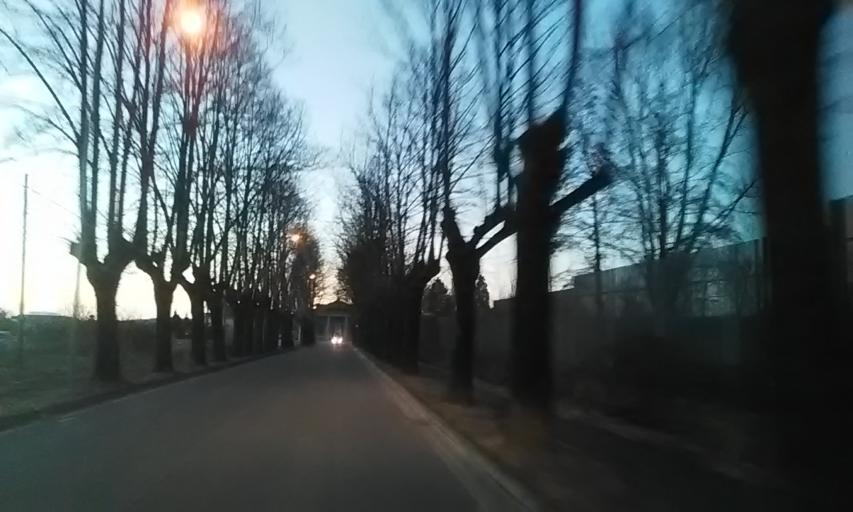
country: IT
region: Piedmont
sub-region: Provincia di Biella
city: Occhieppo Inferiore
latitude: 45.5524
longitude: 8.0371
